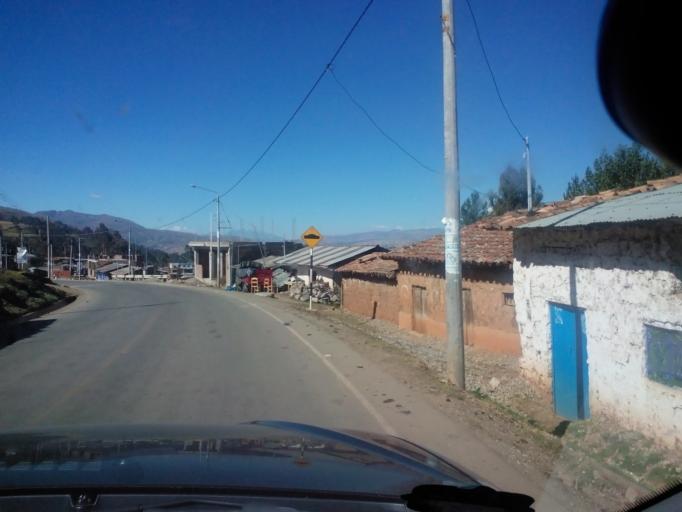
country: PE
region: Apurimac
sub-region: Provincia de Andahuaylas
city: Talavera
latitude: -13.6536
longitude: -73.5328
